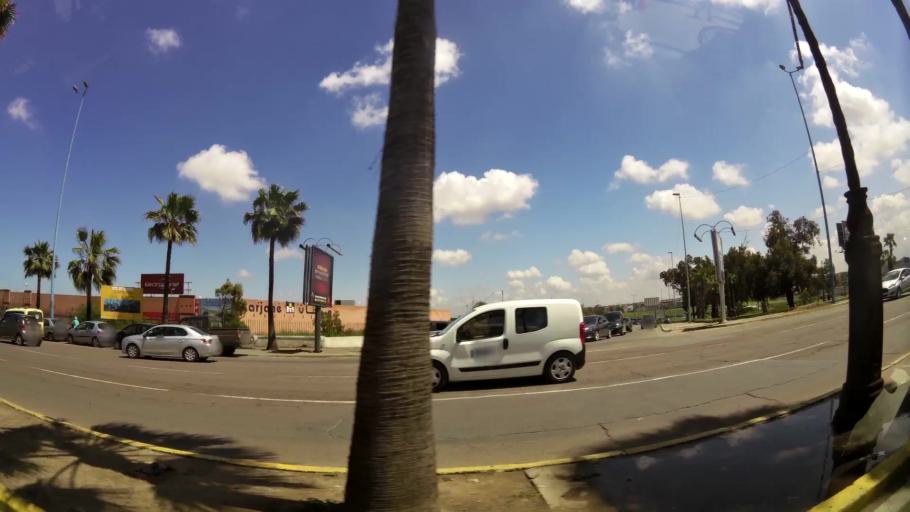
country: MA
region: Grand Casablanca
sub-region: Casablanca
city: Casablanca
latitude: 33.5604
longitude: -7.5945
